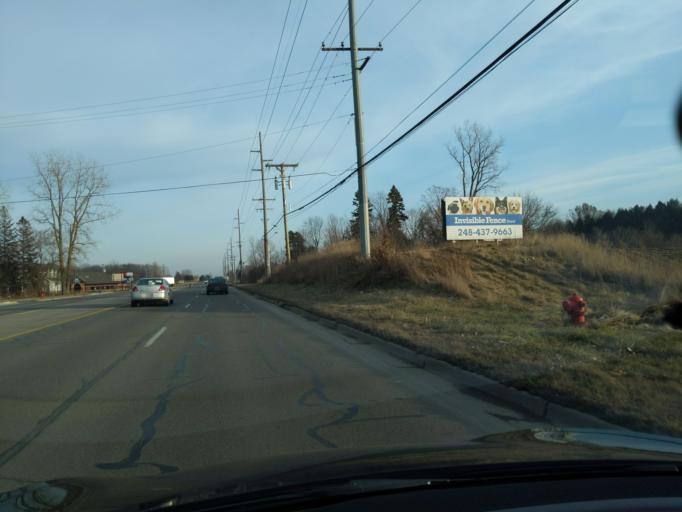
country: US
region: Michigan
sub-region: Livingston County
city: Brighton
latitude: 42.5735
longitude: -83.8312
